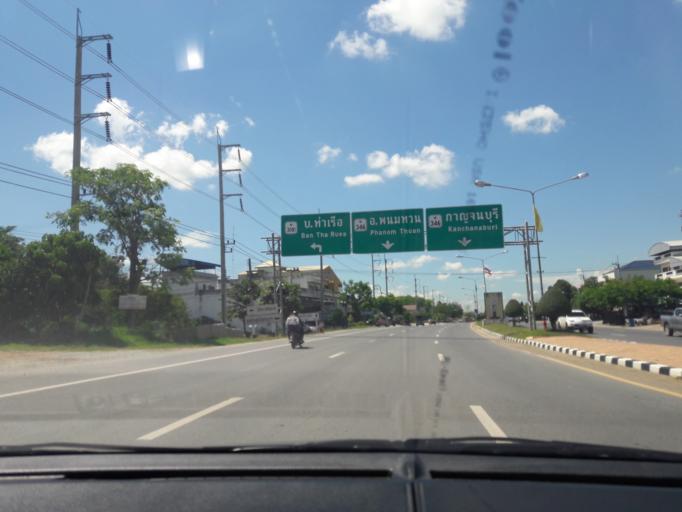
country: TH
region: Kanchanaburi
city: Tha Maka
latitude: 14.0375
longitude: 99.7922
